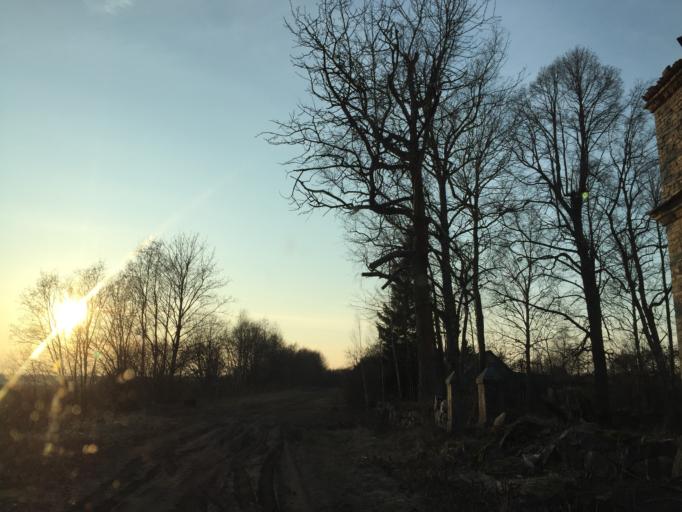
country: EE
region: Laeaene
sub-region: Lihula vald
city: Lihula
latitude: 58.5323
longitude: 24.0423
